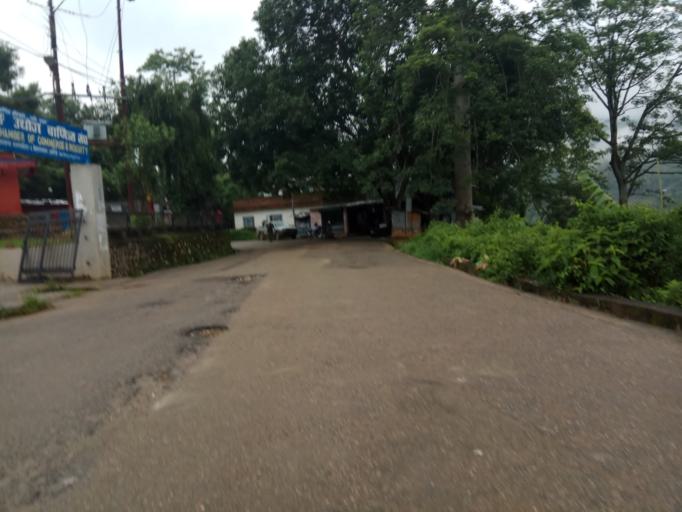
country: NP
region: Central Region
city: Kirtipur
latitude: 27.9097
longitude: 84.8993
